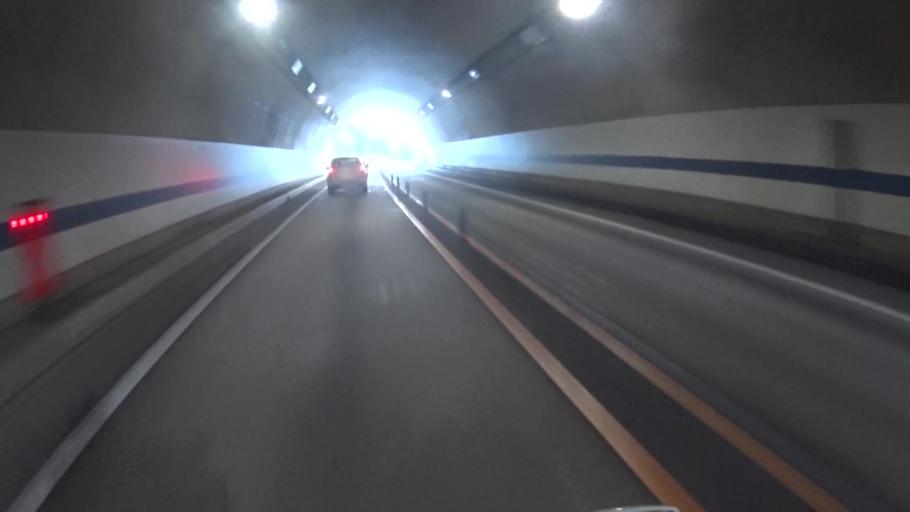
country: JP
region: Kyoto
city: Ayabe
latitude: 35.3676
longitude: 135.2839
